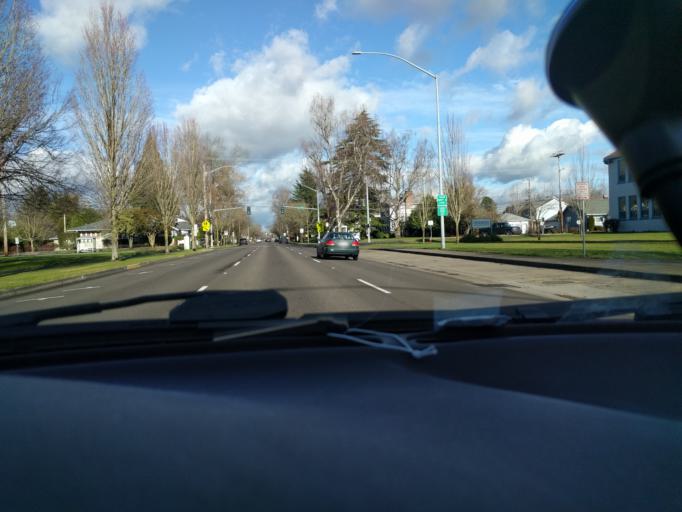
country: US
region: Oregon
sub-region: Marion County
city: Salem
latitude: 44.9457
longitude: -123.0250
